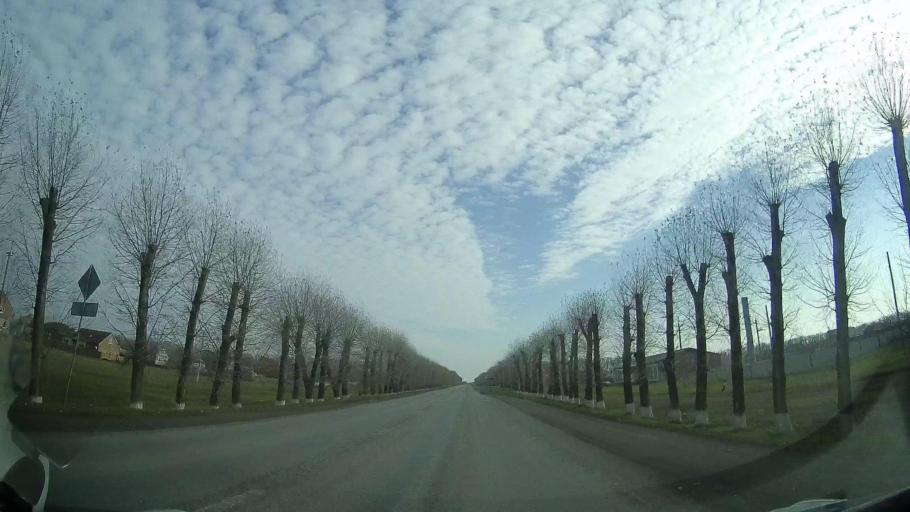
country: RU
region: Rostov
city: Tselina
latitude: 46.5285
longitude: 41.0529
